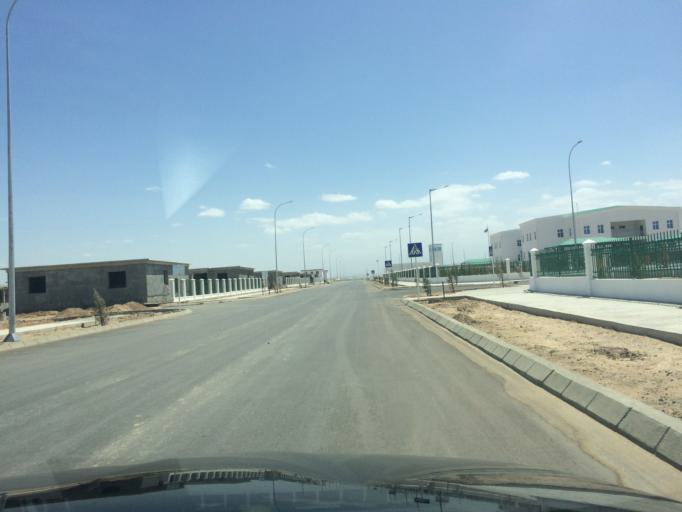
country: TM
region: Ahal
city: Abadan
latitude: 38.0971
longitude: 58.2939
